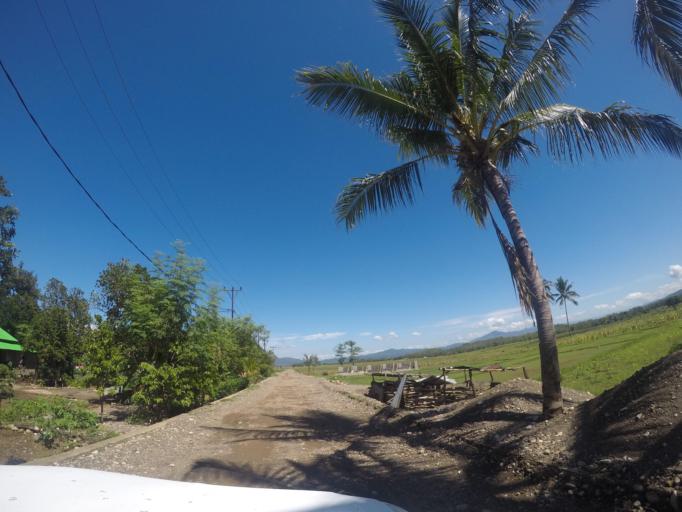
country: TL
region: Bobonaro
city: Maliana
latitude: -8.9827
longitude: 125.2100
